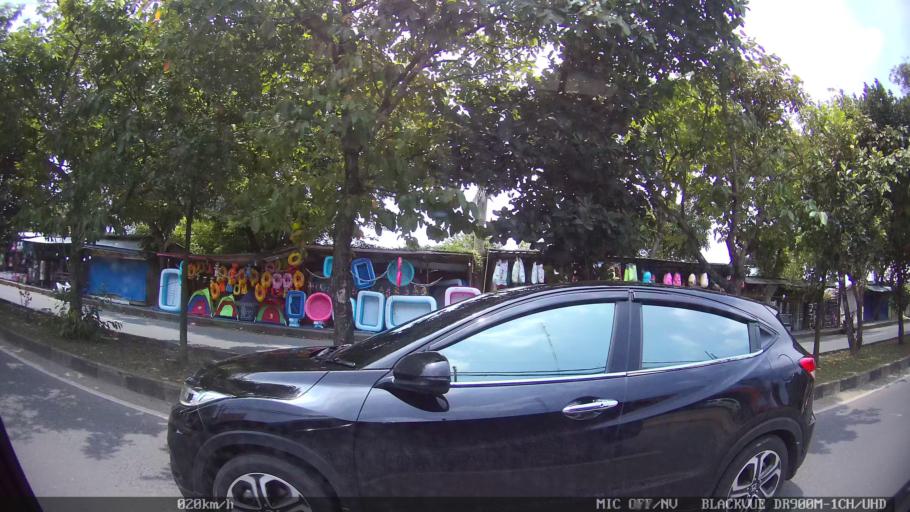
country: ID
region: Lampung
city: Kedaton
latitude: -5.3819
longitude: 105.2760
